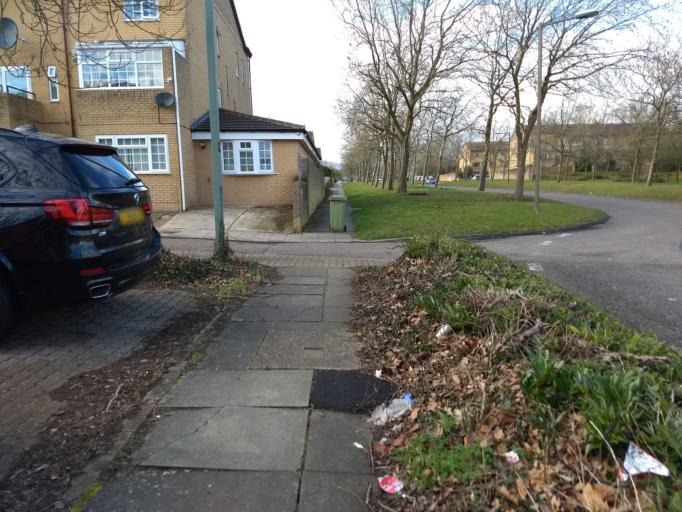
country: GB
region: England
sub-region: Milton Keynes
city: Milton Keynes
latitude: 52.0349
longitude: -0.7420
